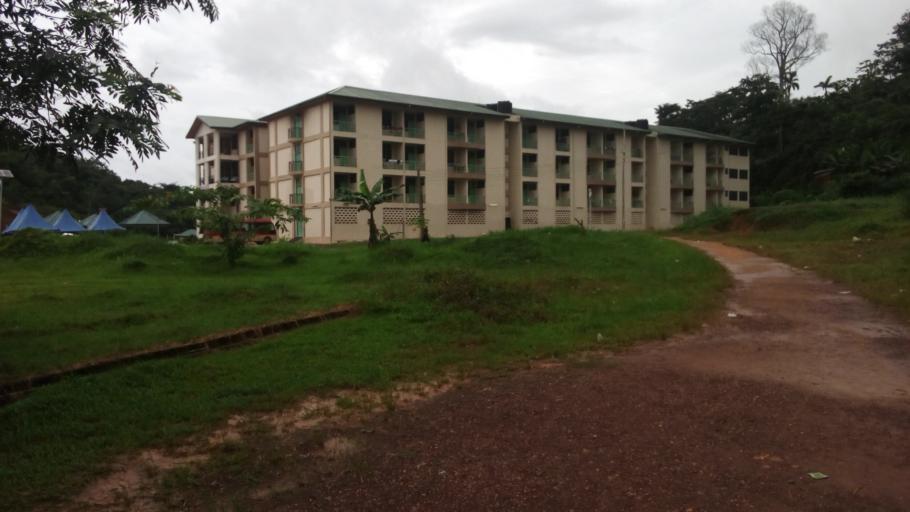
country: GH
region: Western
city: Tarkwa
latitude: 5.2990
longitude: -2.0030
